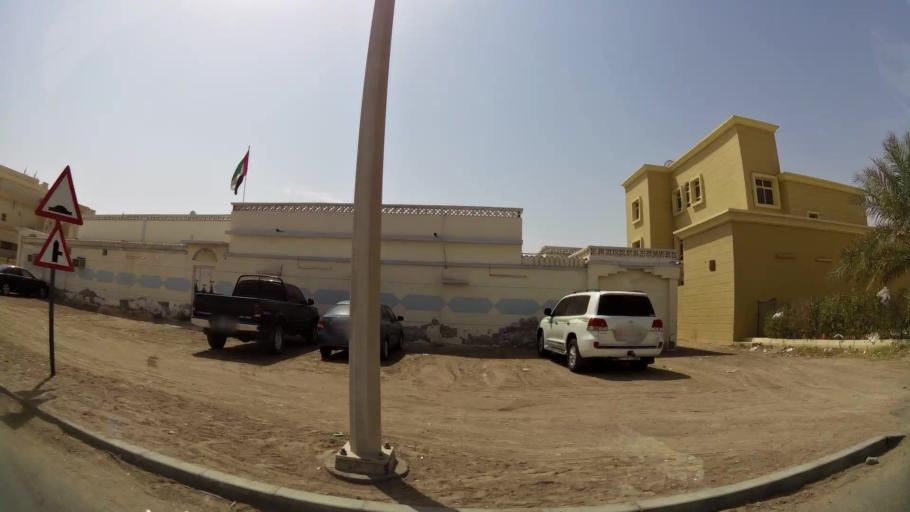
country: AE
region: Abu Dhabi
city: Abu Dhabi
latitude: 24.2962
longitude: 54.6459
